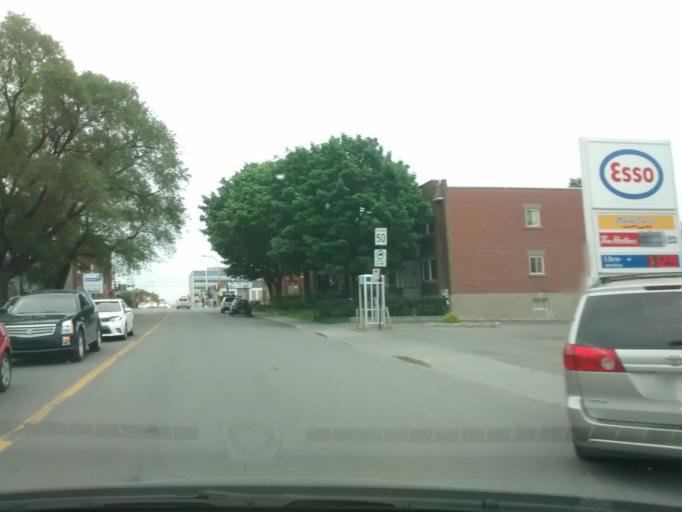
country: CA
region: Quebec
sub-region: Montreal
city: Montreal
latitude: 45.5464
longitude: -73.5862
